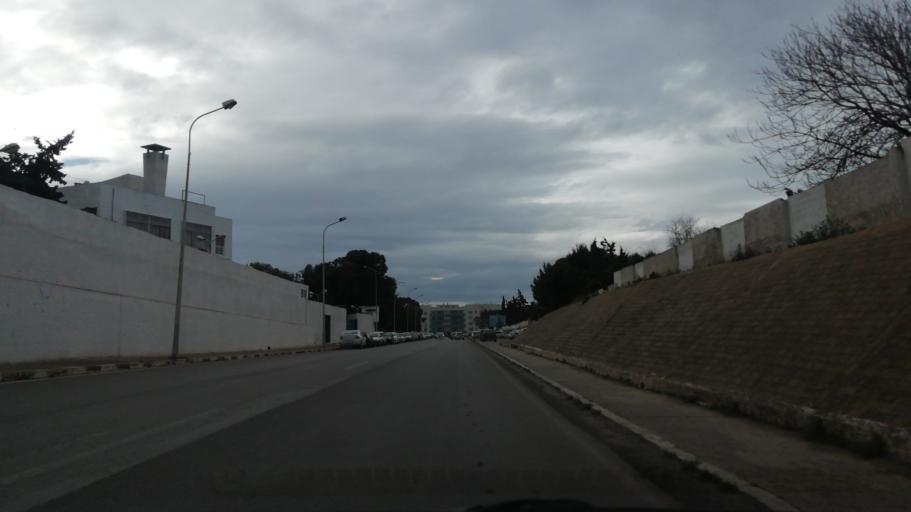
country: DZ
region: Oran
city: Oran
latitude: 35.7000
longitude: -0.6135
